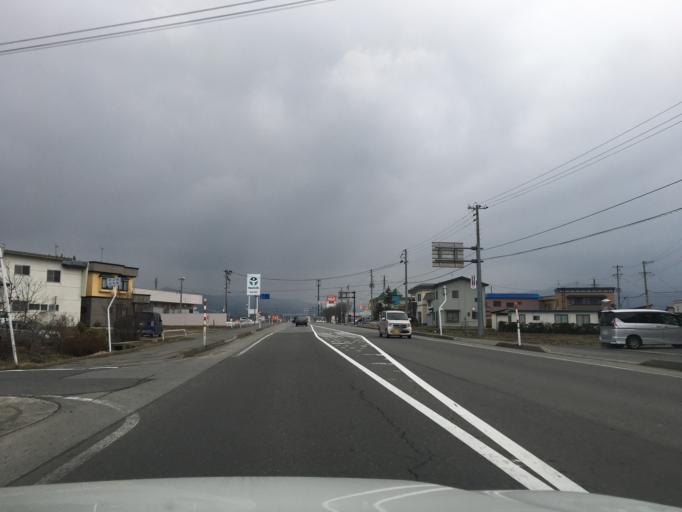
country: JP
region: Aomori
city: Kuroishi
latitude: 40.5838
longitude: 140.5687
